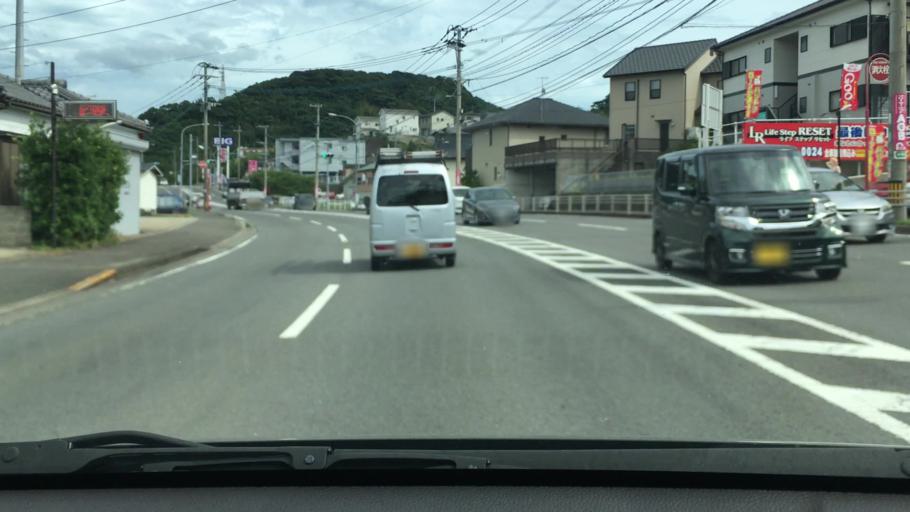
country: JP
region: Nagasaki
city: Togitsu
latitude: 32.8366
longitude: 129.8379
